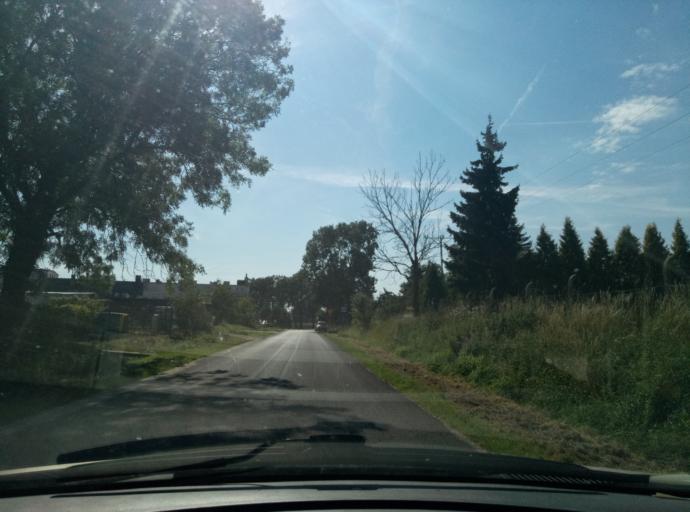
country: PL
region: Kujawsko-Pomorskie
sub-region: Powiat brodnicki
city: Jablonowo Pomorskie
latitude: 53.3879
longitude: 19.1693
